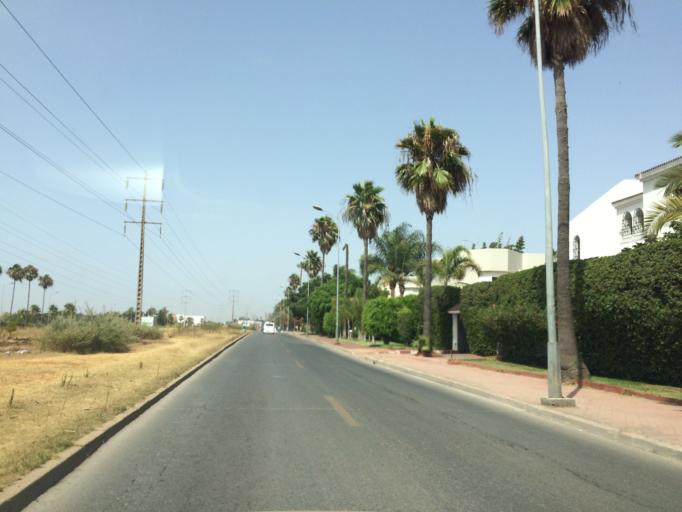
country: MA
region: Rabat-Sale-Zemmour-Zaer
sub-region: Skhirate-Temara
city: Temara
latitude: 33.9645
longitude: -6.8709
